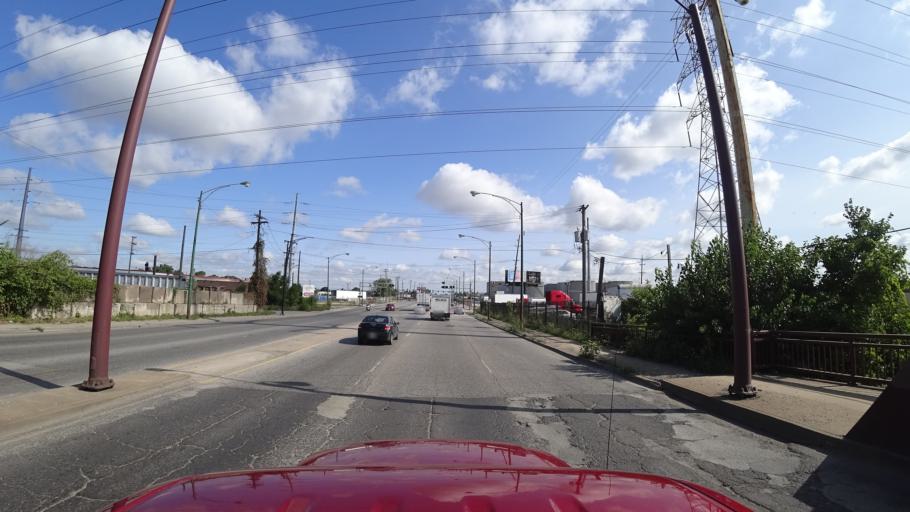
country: US
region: Illinois
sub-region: Cook County
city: Cicero
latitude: 41.8198
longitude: -87.7434
